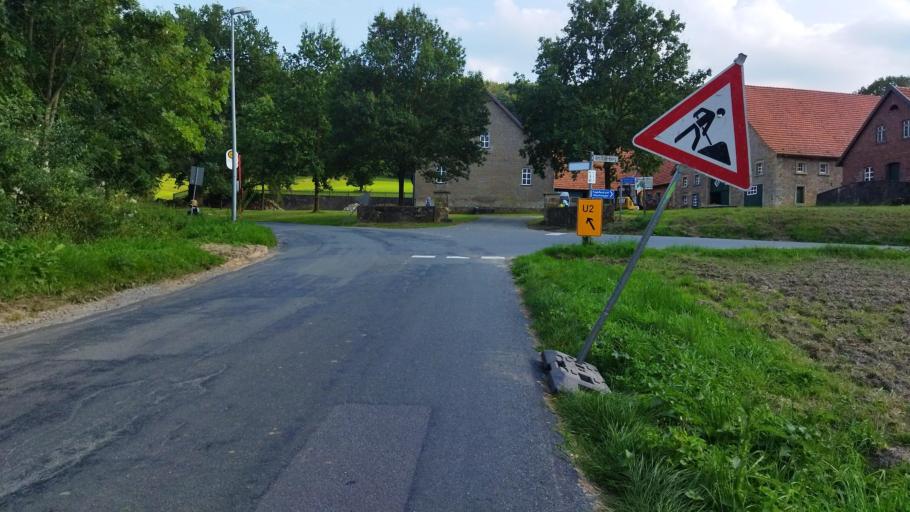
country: DE
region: Lower Saxony
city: Hagen
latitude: 52.2006
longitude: 7.9986
